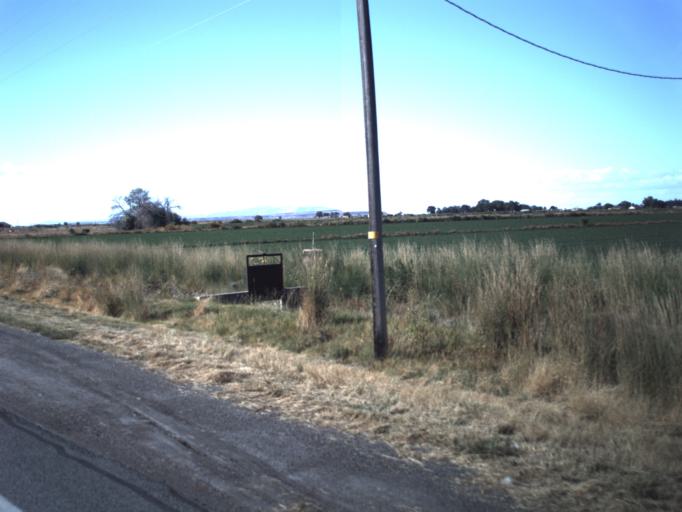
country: US
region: Utah
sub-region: Millard County
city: Delta
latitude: 39.3304
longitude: -112.6523
